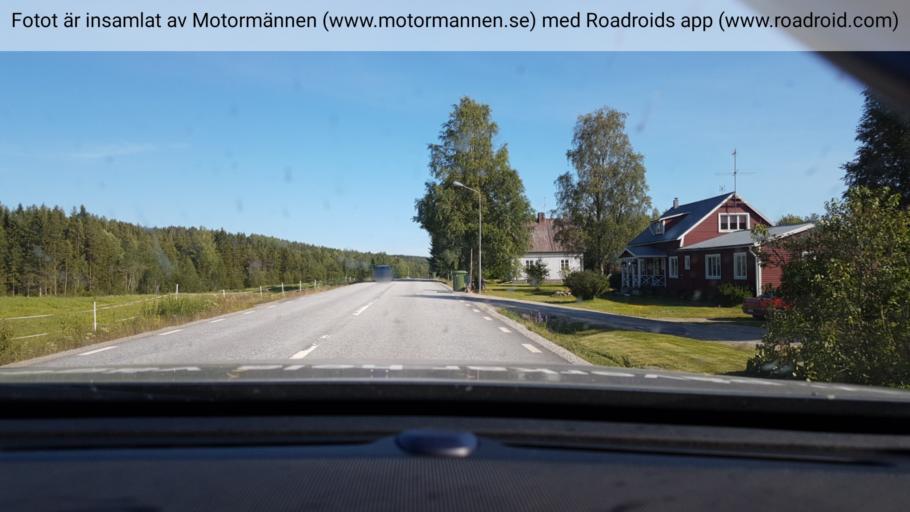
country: SE
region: Vaesterbotten
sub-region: Vindelns Kommun
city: Vindeln
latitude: 64.1599
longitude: 19.5025
